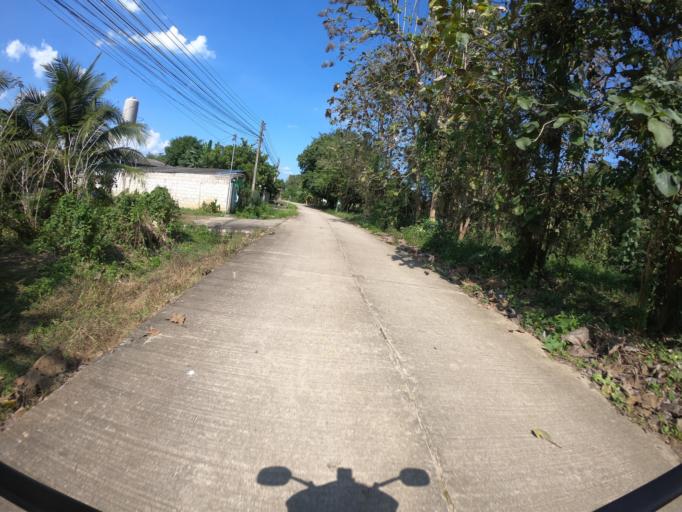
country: TH
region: Chiang Mai
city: San Sai
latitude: 18.8716
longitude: 98.9763
